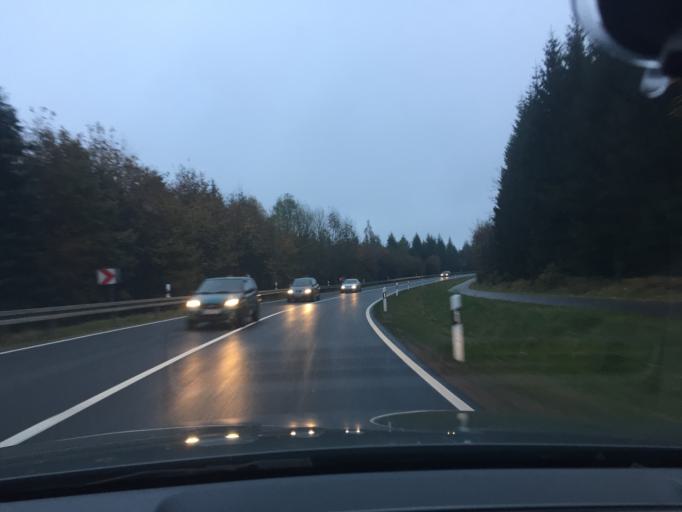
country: DE
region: Saxony
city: Altenberg
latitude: 50.7697
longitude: 13.7388
